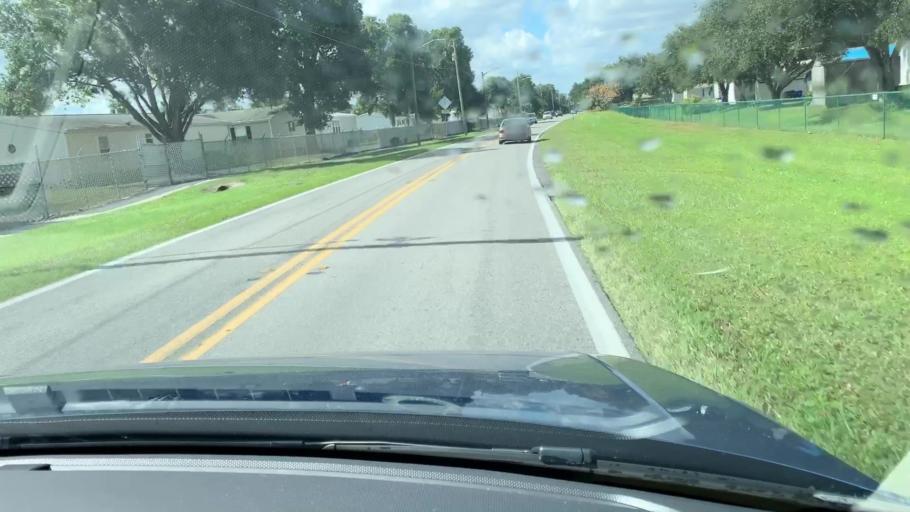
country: US
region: Florida
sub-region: Polk County
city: Winston
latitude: 28.0312
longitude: -81.9819
